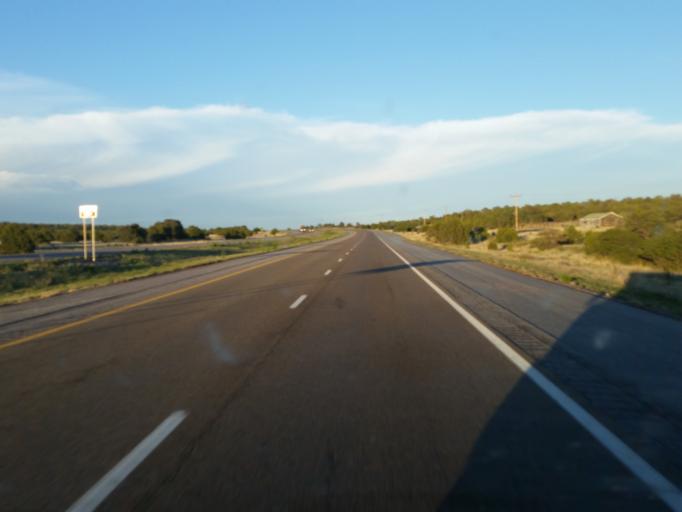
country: US
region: New Mexico
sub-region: Torrance County
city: Moriarty
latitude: 35.0021
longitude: -105.5588
